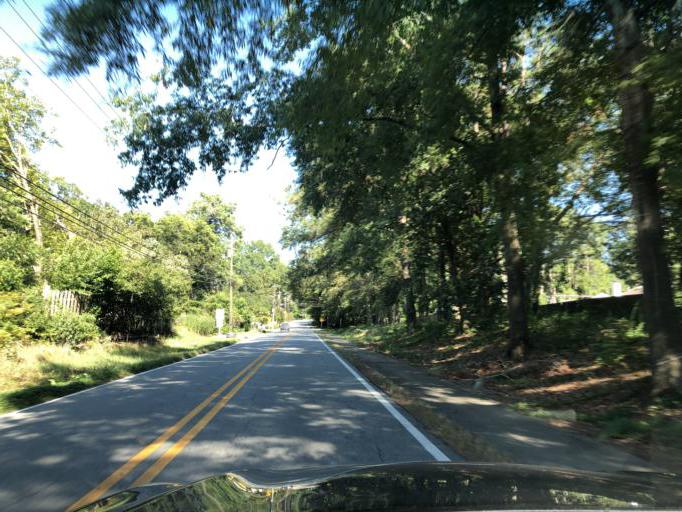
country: US
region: Georgia
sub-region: Muscogee County
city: Columbus
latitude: 32.5068
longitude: -84.9177
